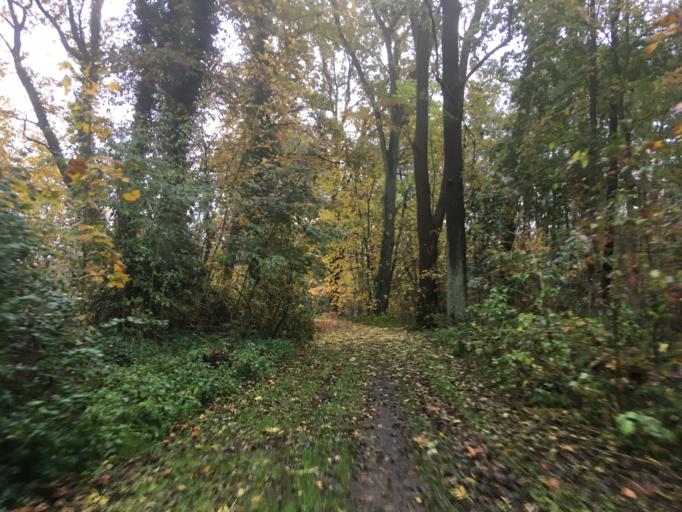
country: DE
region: Brandenburg
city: Neu Zauche
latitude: 52.0350
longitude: 14.0469
